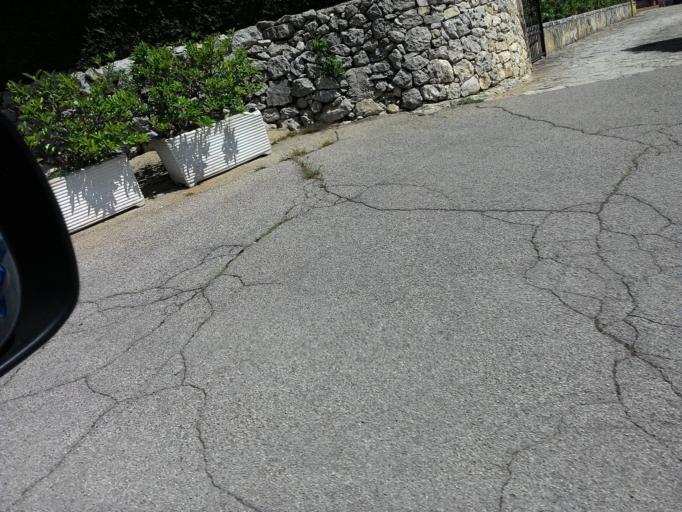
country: IT
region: Apulia
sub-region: Provincia di Bari
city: Putignano
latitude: 40.8361
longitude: 17.1452
